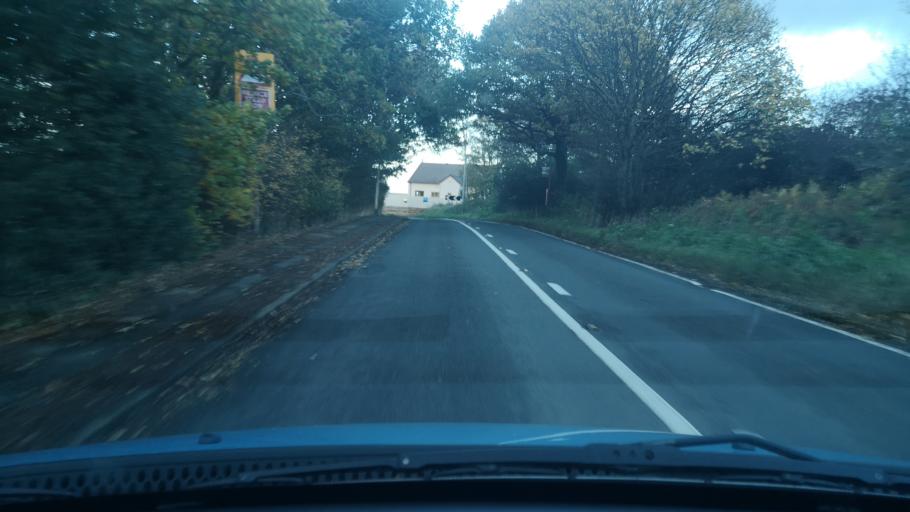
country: GB
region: England
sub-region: City and Borough of Wakefield
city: Middlestown
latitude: 53.6363
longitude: -1.5854
